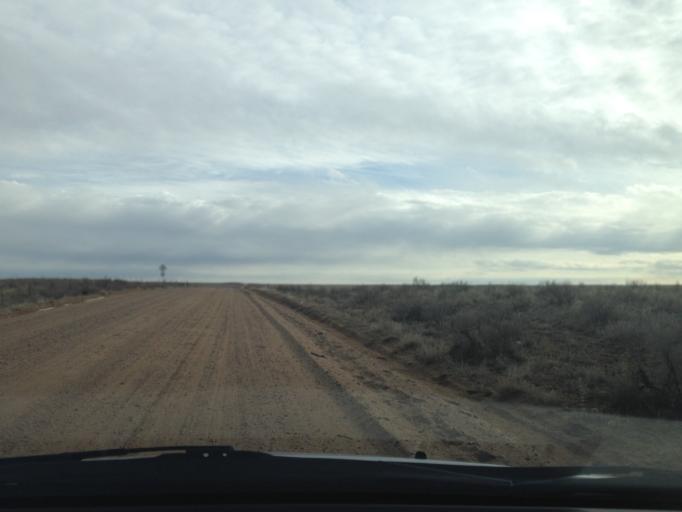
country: US
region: Colorado
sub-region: Weld County
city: Keenesburg
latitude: 40.2700
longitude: -104.2069
